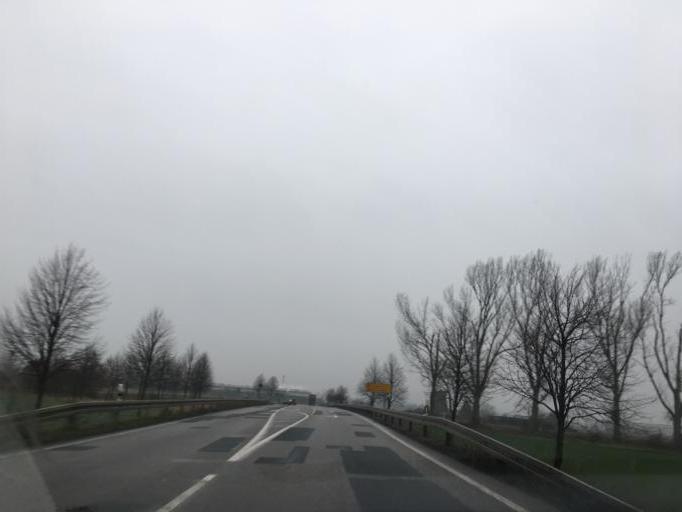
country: DE
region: Saxony-Anhalt
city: Gross Ammensleben
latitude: 52.2208
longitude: 11.5388
